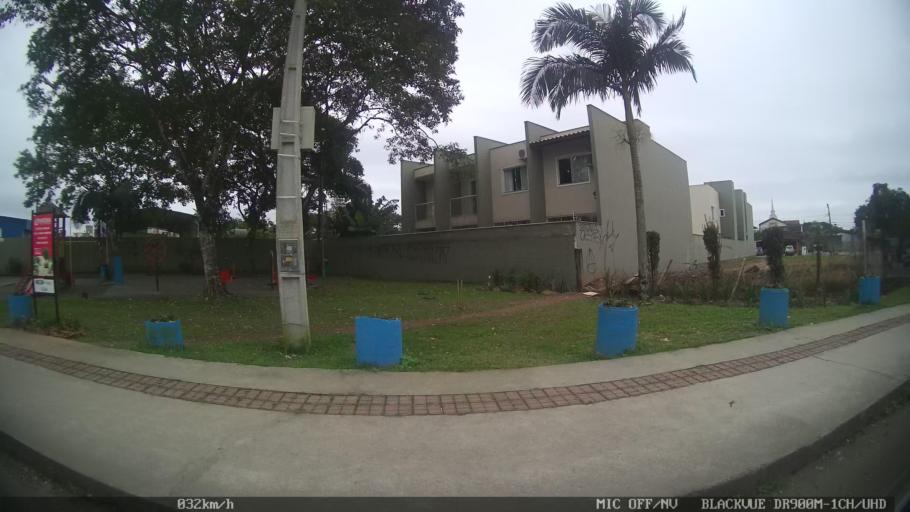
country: BR
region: Santa Catarina
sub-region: Joinville
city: Joinville
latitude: -26.2855
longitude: -48.9025
